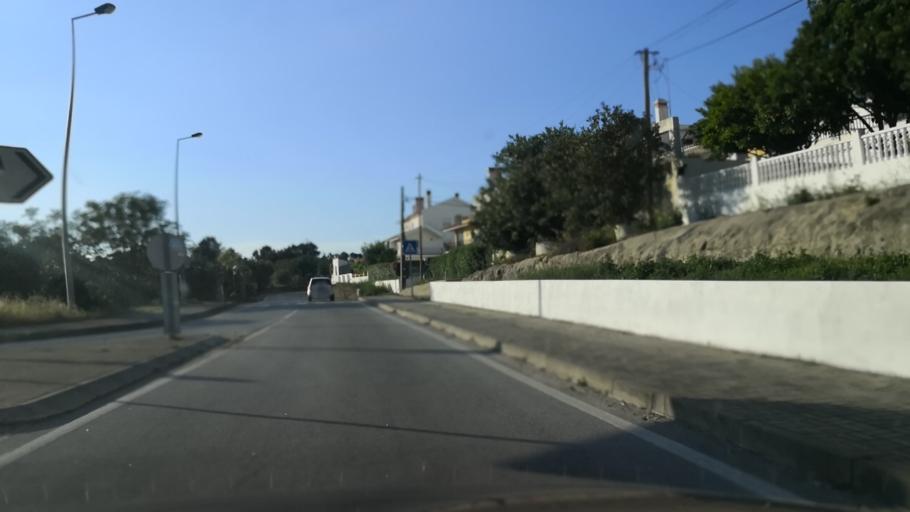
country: PT
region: Portalegre
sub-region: Portalegre
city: Portalegre
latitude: 39.3109
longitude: -7.4405
